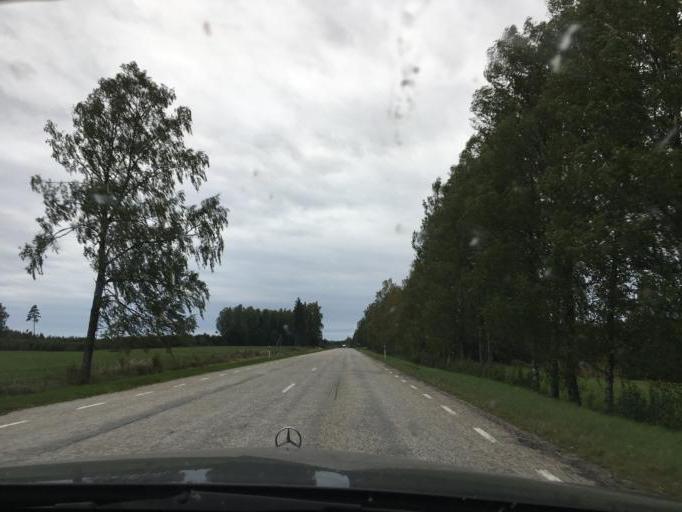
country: LV
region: Aluksnes Rajons
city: Aluksne
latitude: 57.5998
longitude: 27.1619
